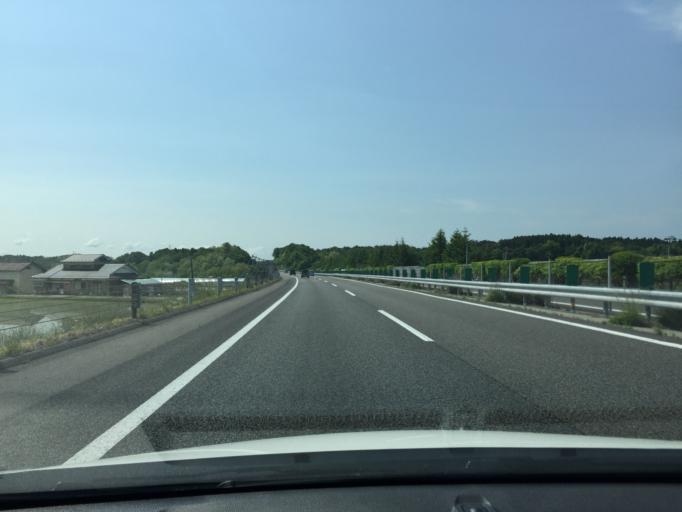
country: JP
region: Fukushima
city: Sukagawa
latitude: 37.3281
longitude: 140.3384
